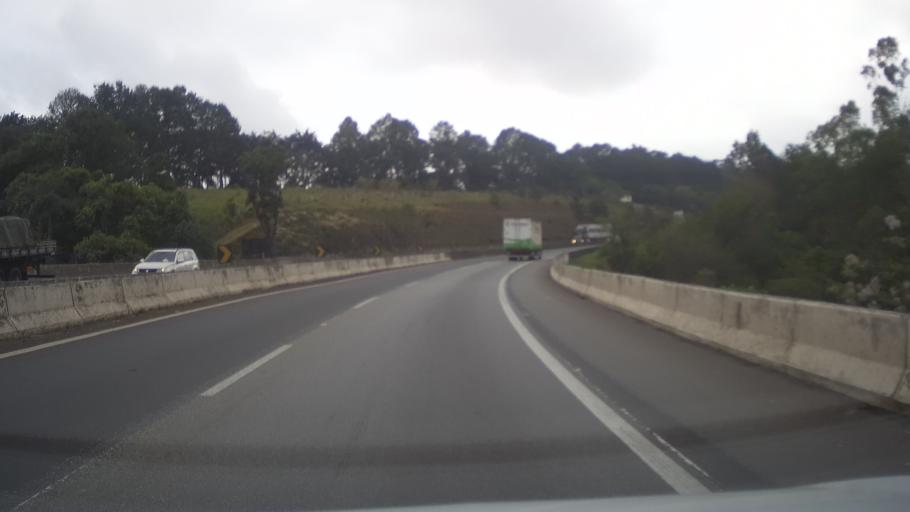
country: BR
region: Minas Gerais
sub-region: Extrema
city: Extrema
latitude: -22.8615
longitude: -46.3441
